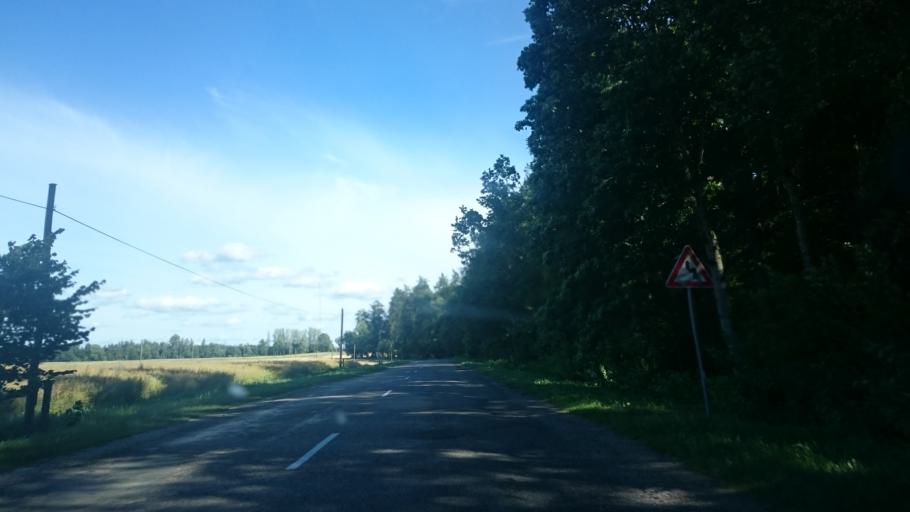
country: LV
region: Aizpute
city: Aizpute
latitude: 56.7246
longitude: 21.7485
